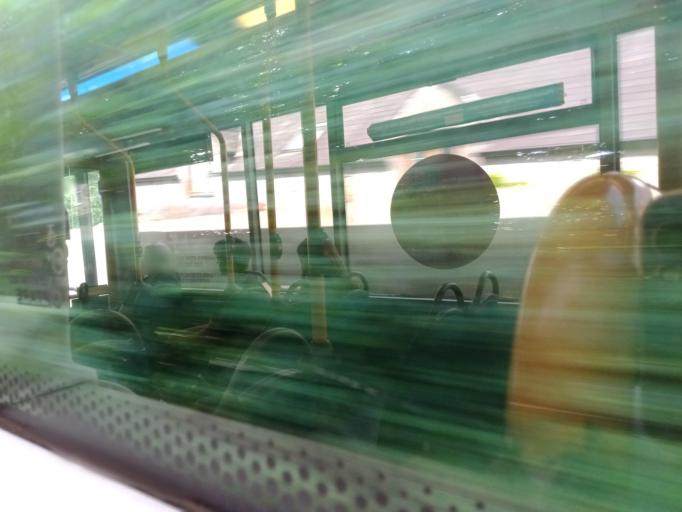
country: GB
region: Wales
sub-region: Anglesey
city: Llangoed
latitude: 53.3018
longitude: -4.0844
